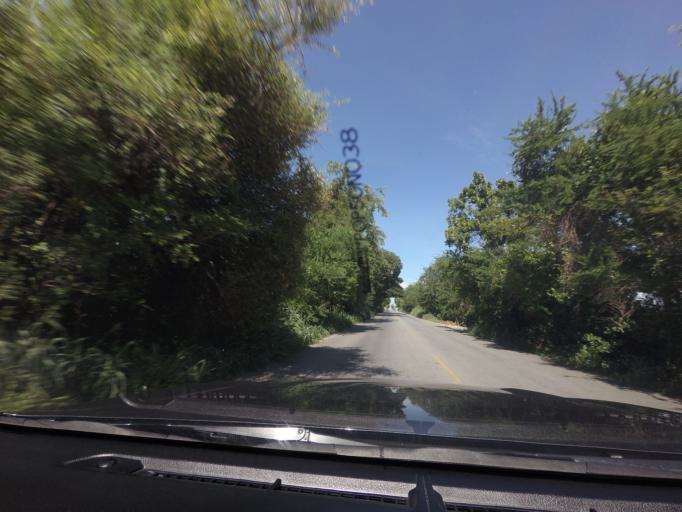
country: TH
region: Suphan Buri
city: Song Phi Nong
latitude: 14.1663
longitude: 99.9168
